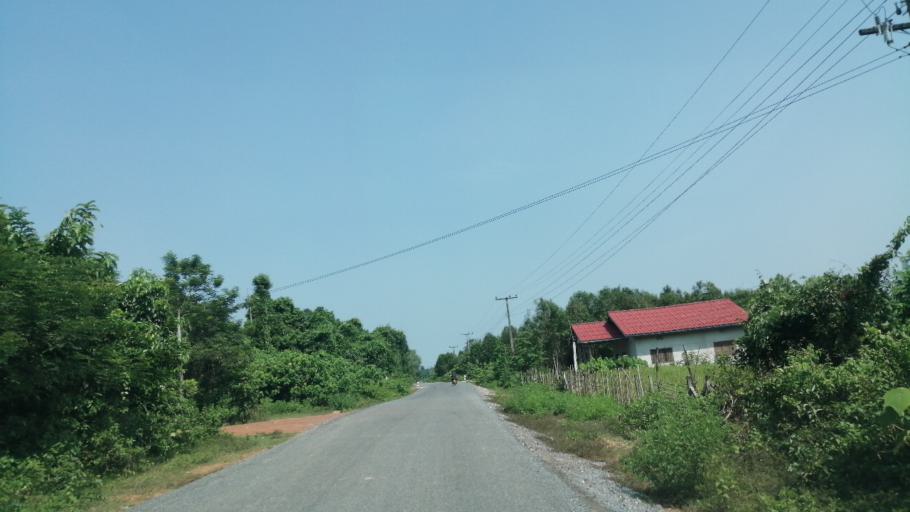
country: LA
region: Bolikhamxai
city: Bolikhan
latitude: 18.4540
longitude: 103.8045
